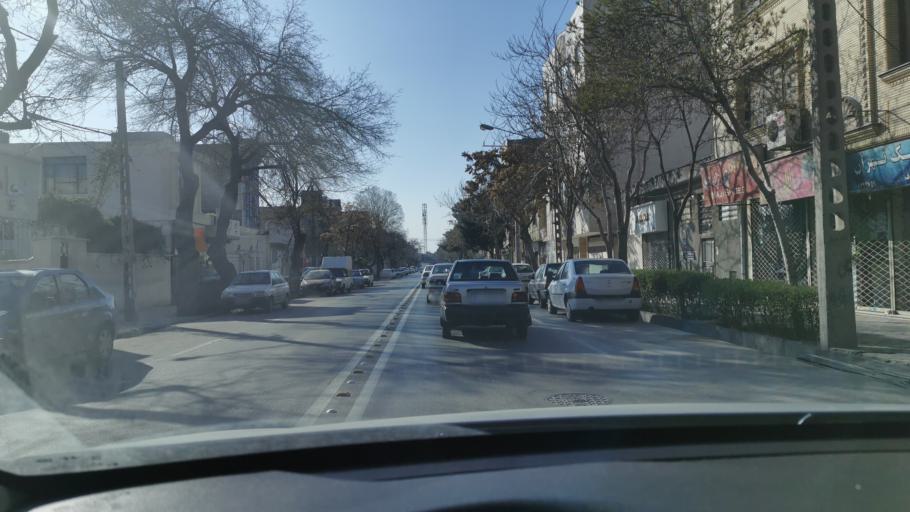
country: IR
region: Razavi Khorasan
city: Mashhad
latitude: 36.2789
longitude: 59.5744
